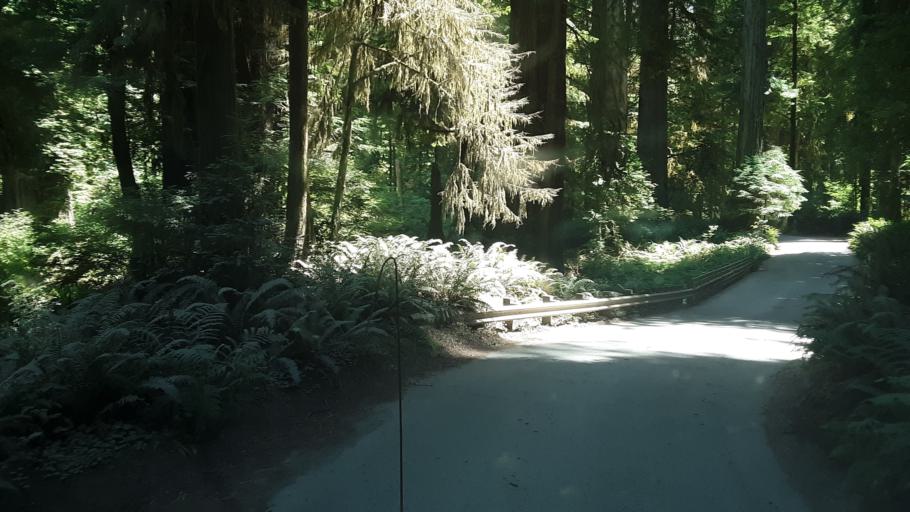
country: US
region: California
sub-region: Del Norte County
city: Bertsch-Oceanview
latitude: 41.8132
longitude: -124.1098
